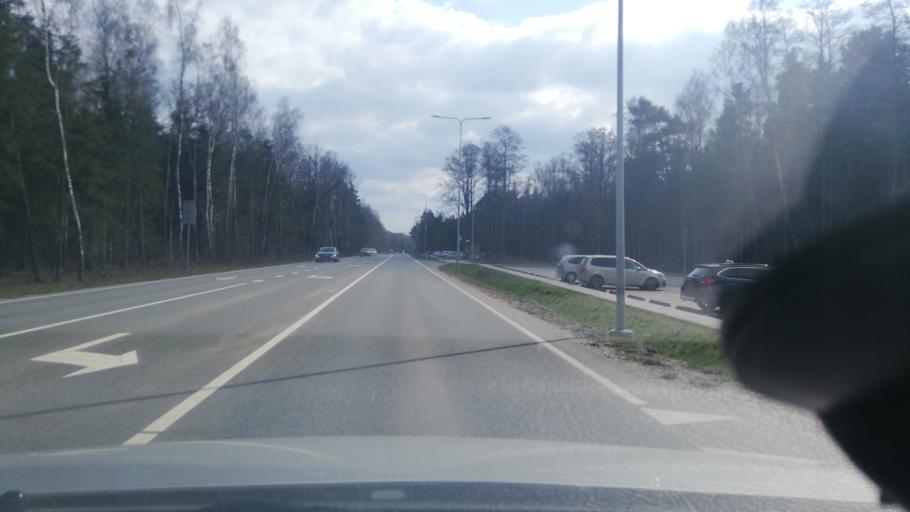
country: LT
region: Klaipedos apskritis
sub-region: Klaipeda
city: Klaipeda
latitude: 55.7490
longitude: 21.0926
